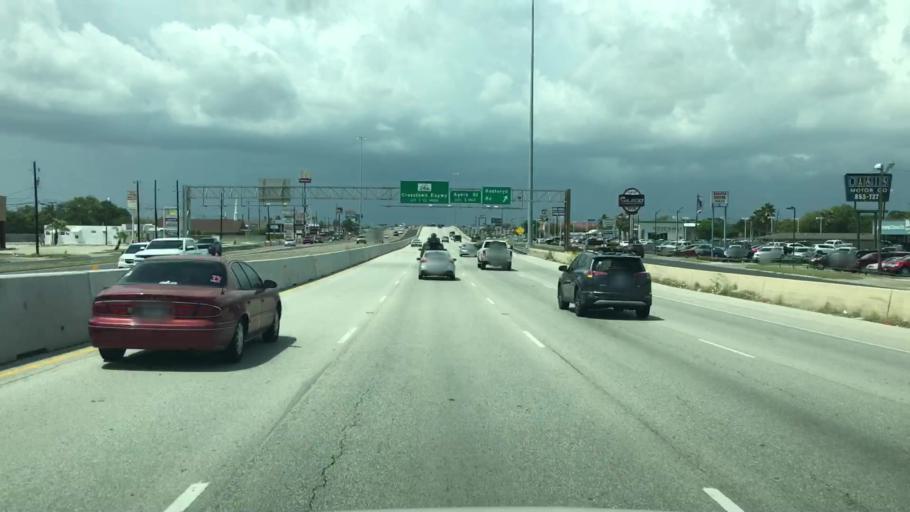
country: US
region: Texas
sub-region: Nueces County
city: Corpus Christi
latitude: 27.7262
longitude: -97.4079
